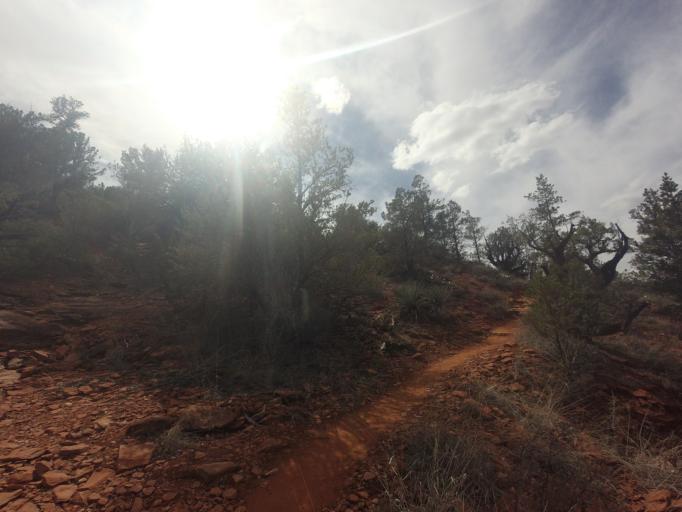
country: US
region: Arizona
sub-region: Yavapai County
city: West Sedona
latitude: 34.8070
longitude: -111.8289
